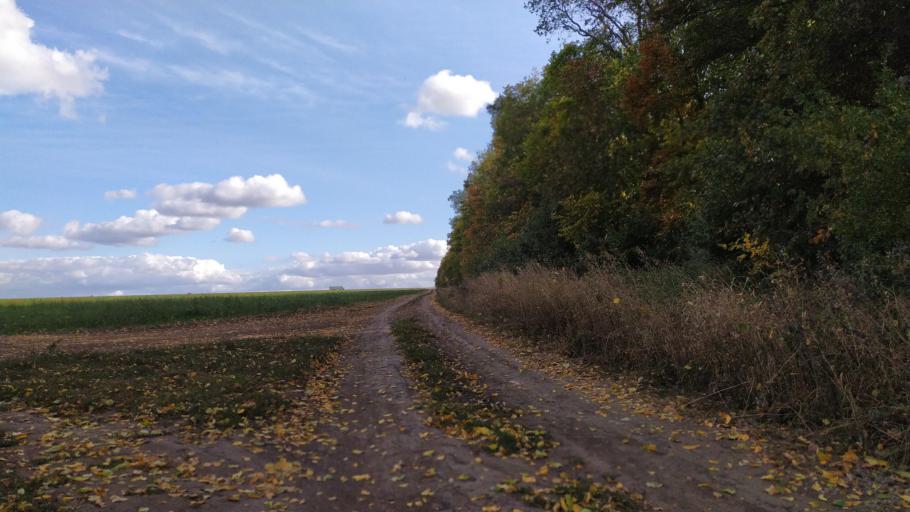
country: RU
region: Kursk
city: Kursk
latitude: 51.6219
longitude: 36.1615
